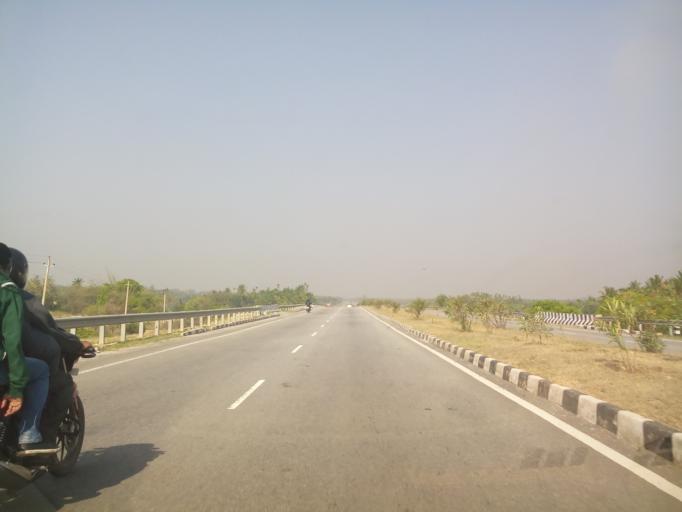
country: IN
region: Karnataka
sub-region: Tumkur
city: Kunigal
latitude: 13.0050
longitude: 77.0077
